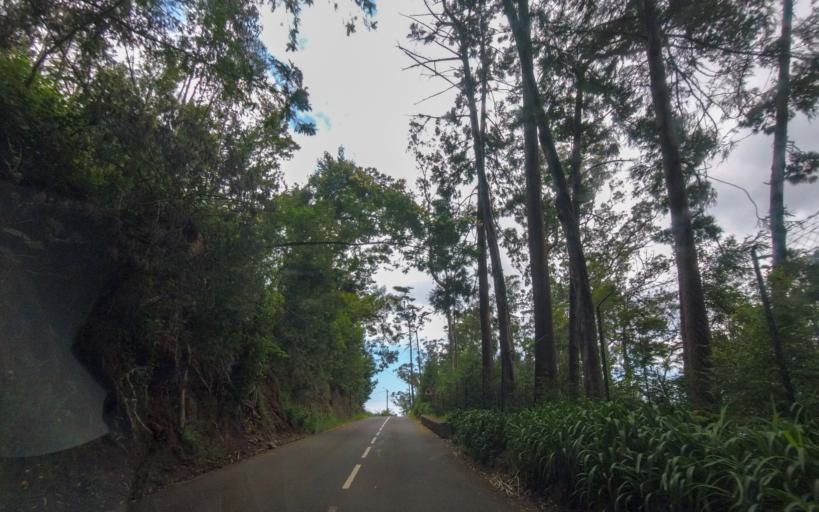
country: PT
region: Madeira
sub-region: Funchal
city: Nossa Senhora do Monte
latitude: 32.6736
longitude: -16.8825
